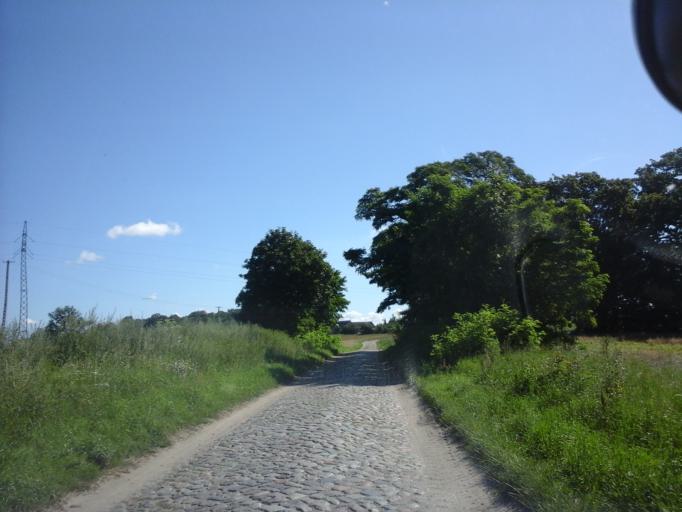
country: PL
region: West Pomeranian Voivodeship
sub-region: Powiat choszczenski
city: Choszczno
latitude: 53.1806
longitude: 15.4414
